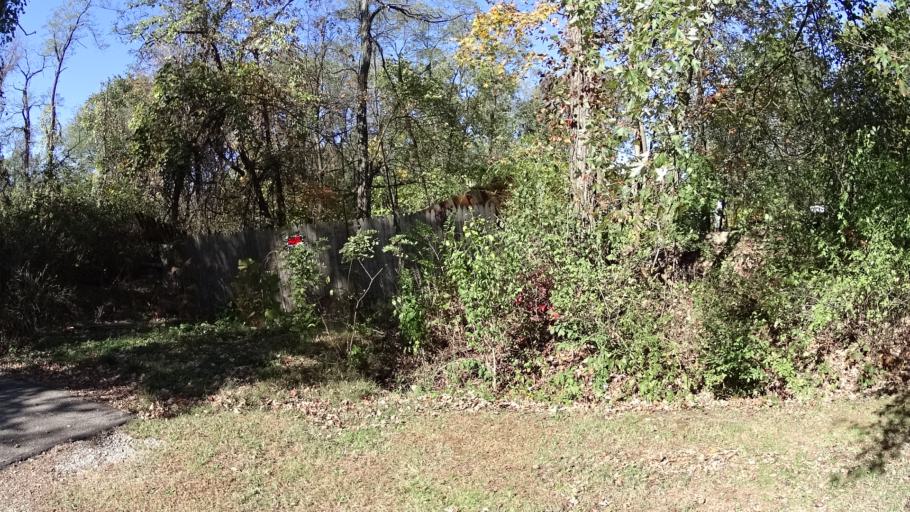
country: US
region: Ohio
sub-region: Lorain County
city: Lorain
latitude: 41.4237
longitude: -82.1443
